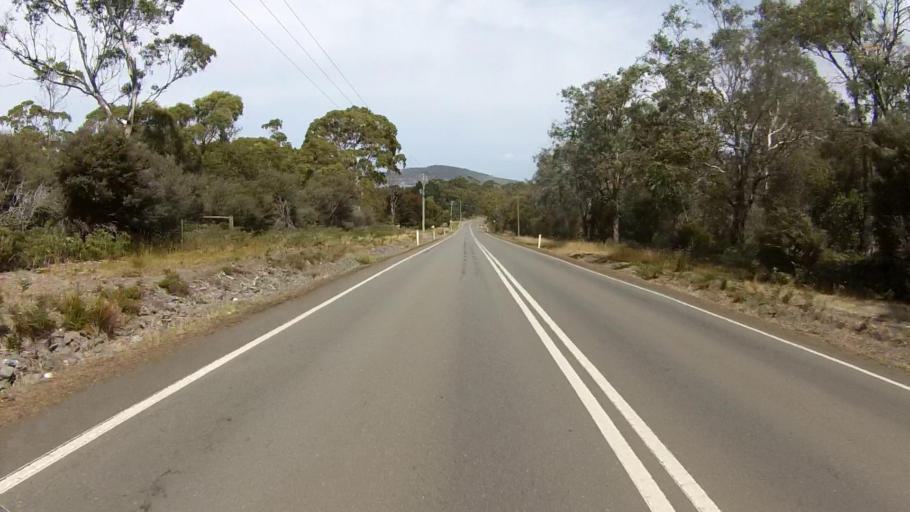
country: AU
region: Tasmania
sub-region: Clarence
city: Sandford
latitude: -43.0113
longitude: 147.4919
